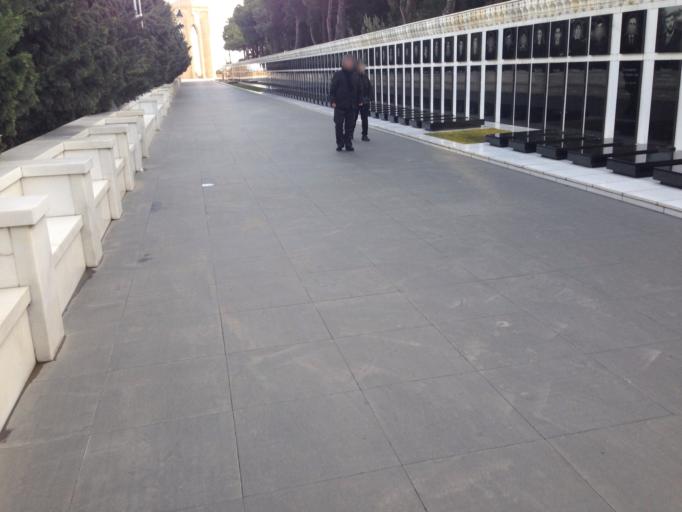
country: AZ
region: Baki
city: Badamdar
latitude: 40.3568
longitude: 49.8284
